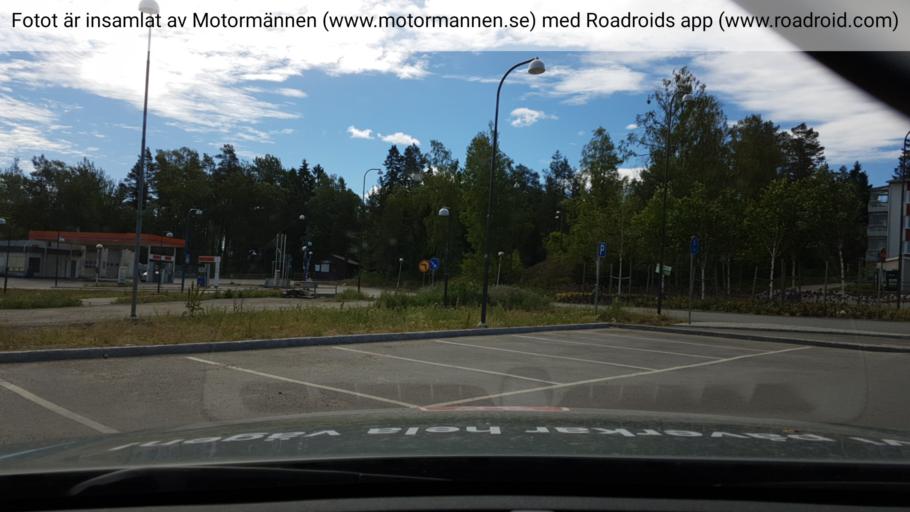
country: SE
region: Stockholm
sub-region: Nynashamns Kommun
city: Osmo
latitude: 58.9826
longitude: 17.8953
